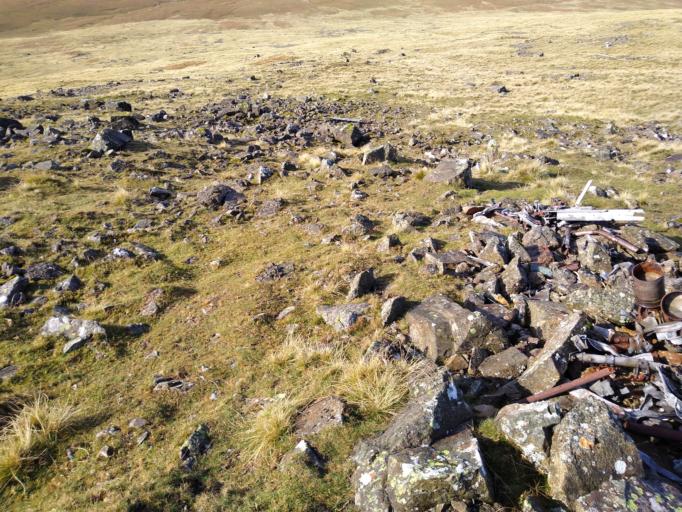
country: GB
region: England
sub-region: Cumbria
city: Keswick
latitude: 54.4357
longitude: -3.2224
